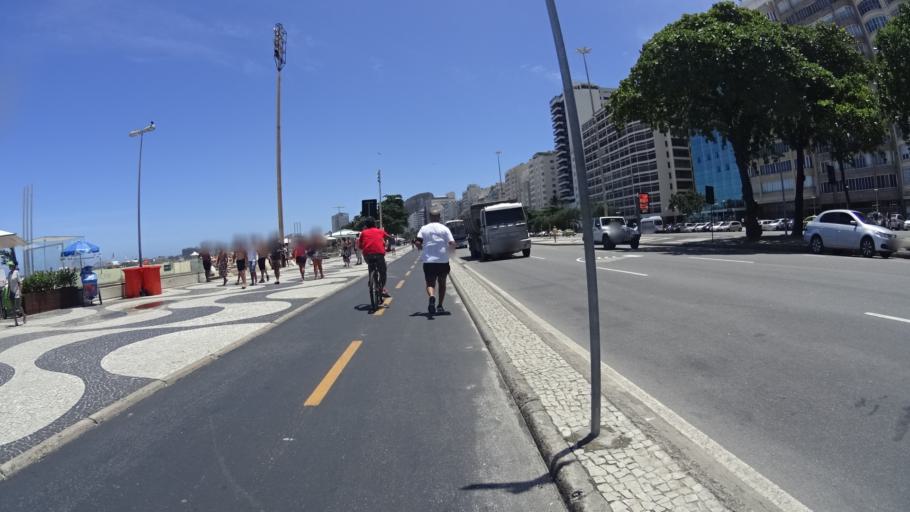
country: BR
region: Rio de Janeiro
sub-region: Rio De Janeiro
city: Rio de Janeiro
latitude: -22.9693
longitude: -43.1799
